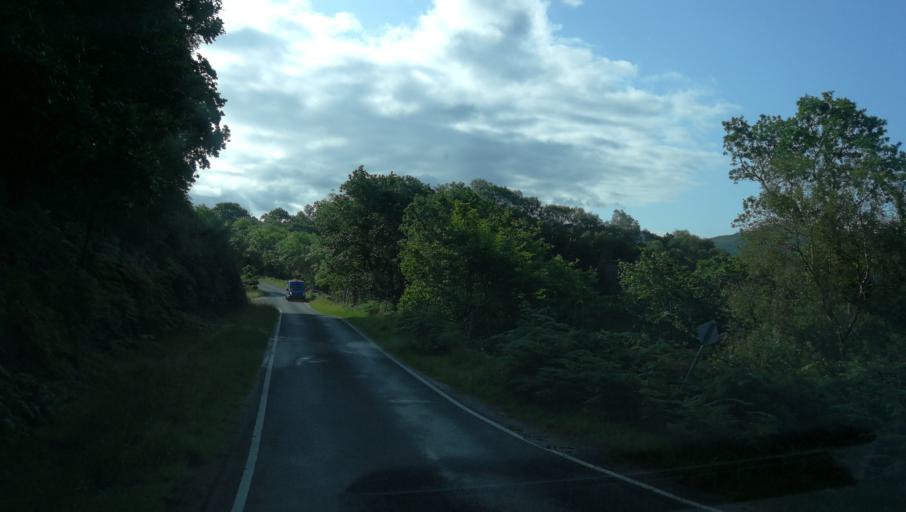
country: GB
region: Scotland
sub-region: Argyll and Bute
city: Isle Of Mull
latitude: 56.6808
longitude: -5.8573
